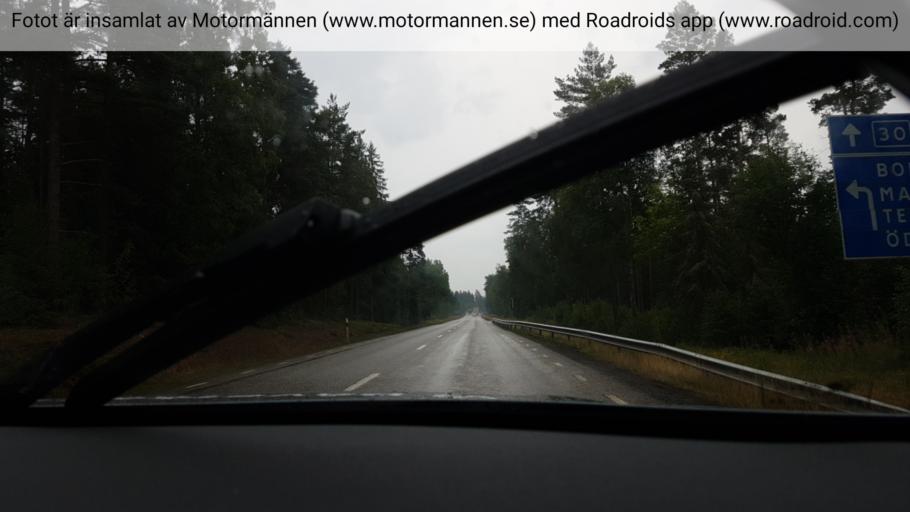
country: SE
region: Joenkoeping
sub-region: Jonkopings Kommun
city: Odensjo
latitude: 57.6115
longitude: 14.2100
